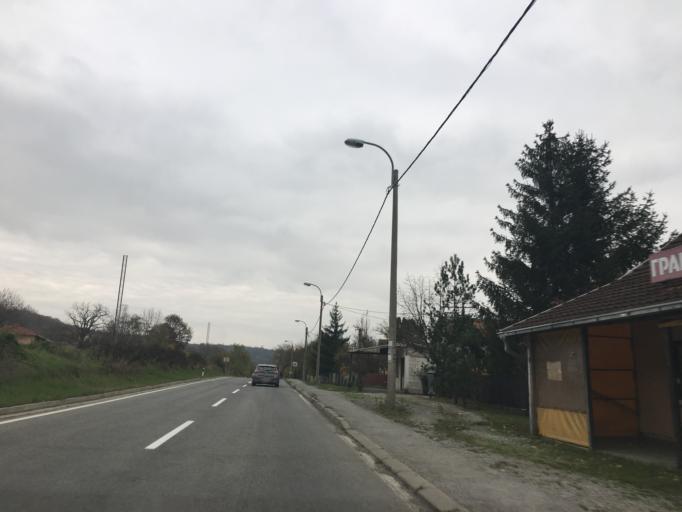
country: RS
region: Central Serbia
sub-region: Raski Okrug
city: Kraljevo
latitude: 43.7236
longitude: 20.7669
